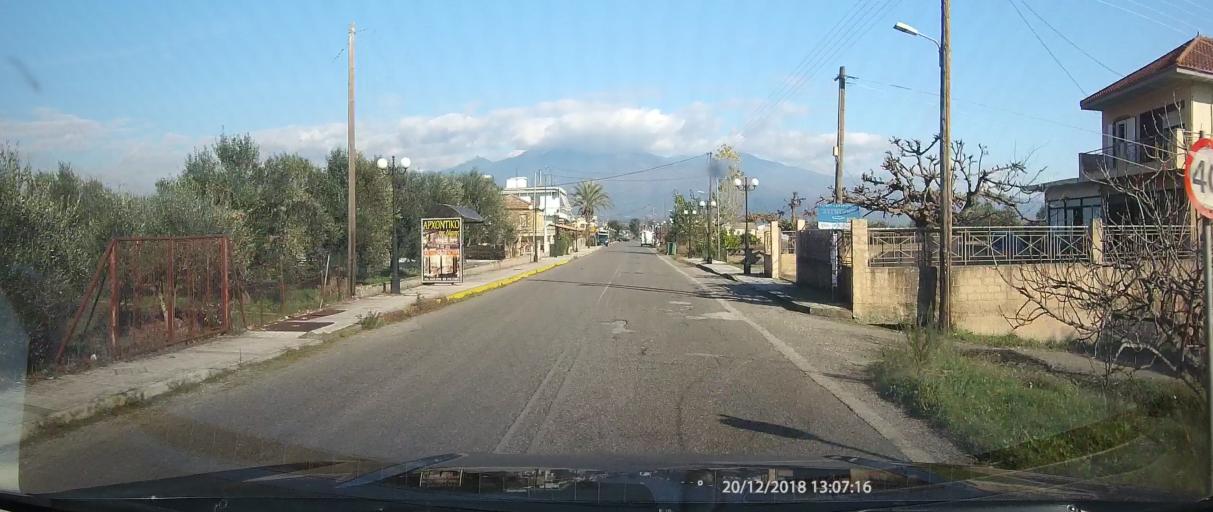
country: GR
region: West Greece
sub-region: Nomos Aitolias kai Akarnanias
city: Panaitolion
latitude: 38.5875
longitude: 21.4546
